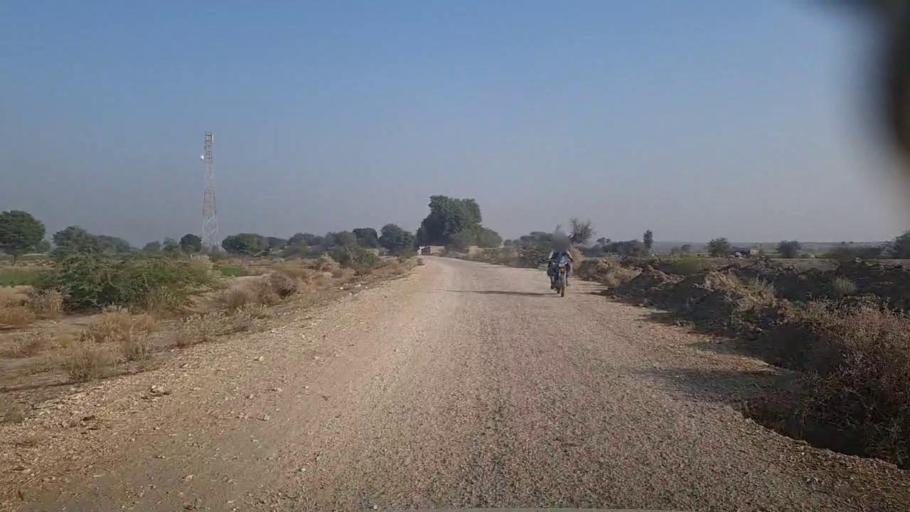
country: PK
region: Sindh
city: Karaundi
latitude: 26.7209
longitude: 68.4933
